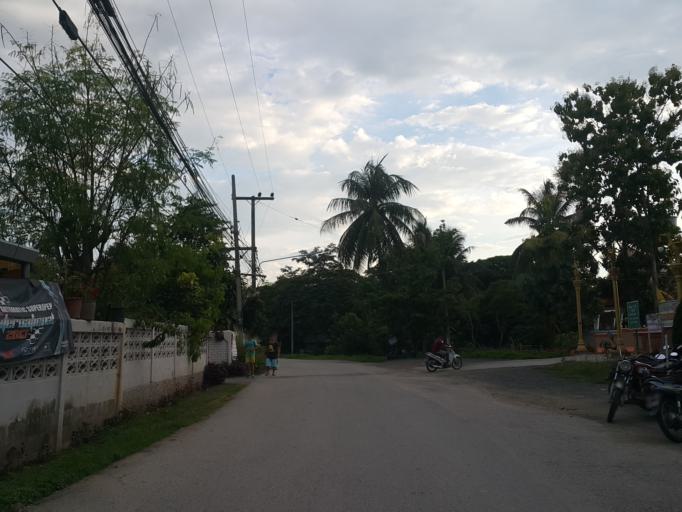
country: TH
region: Chiang Mai
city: San Sai
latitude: 18.8629
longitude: 99.1020
